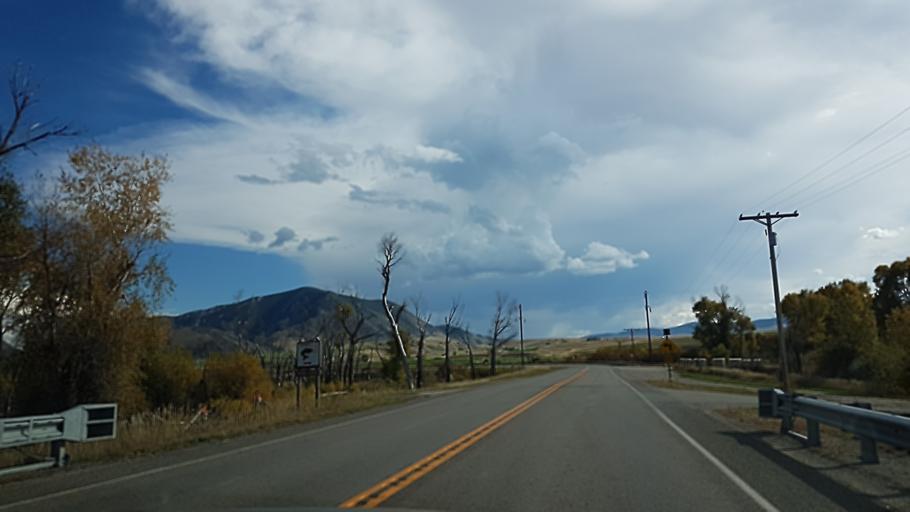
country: US
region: Montana
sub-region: Jefferson County
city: Whitehall
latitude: 45.8543
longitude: -111.9506
